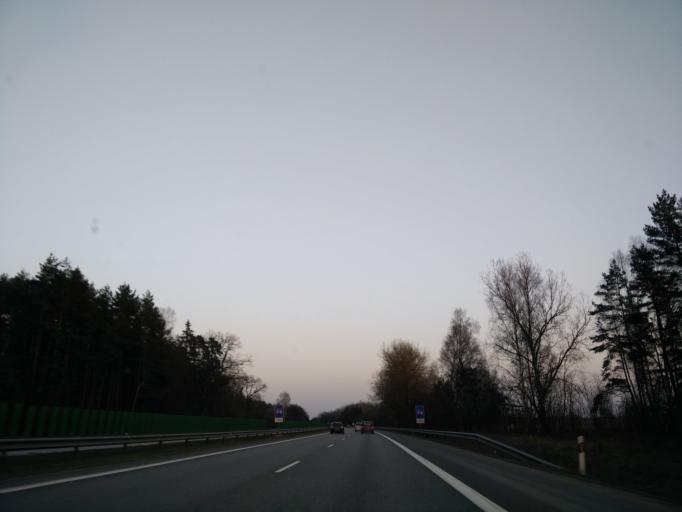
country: LT
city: Lentvaris
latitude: 54.6992
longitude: 25.0127
